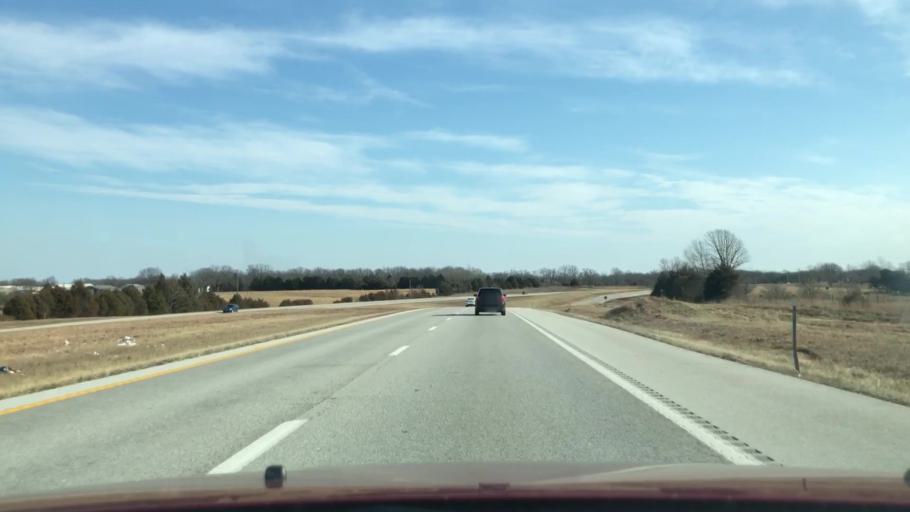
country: US
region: Missouri
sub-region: Webster County
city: Seymour
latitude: 37.1306
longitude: -92.7263
